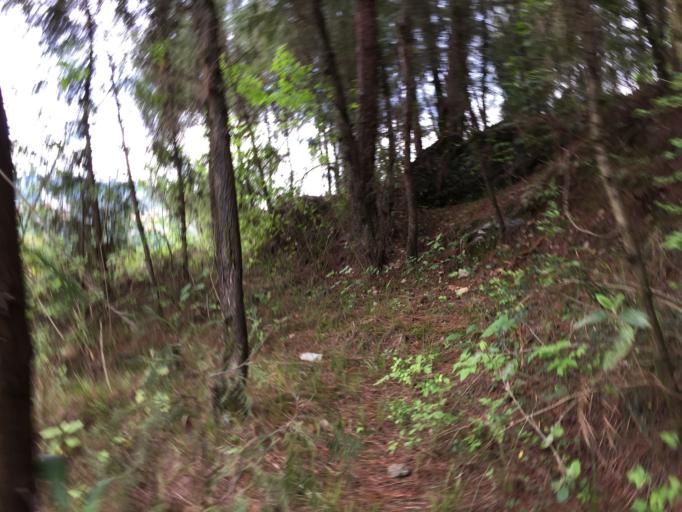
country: CN
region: Guizhou Sheng
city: Xujiaba
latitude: 27.6779
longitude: 108.0870
